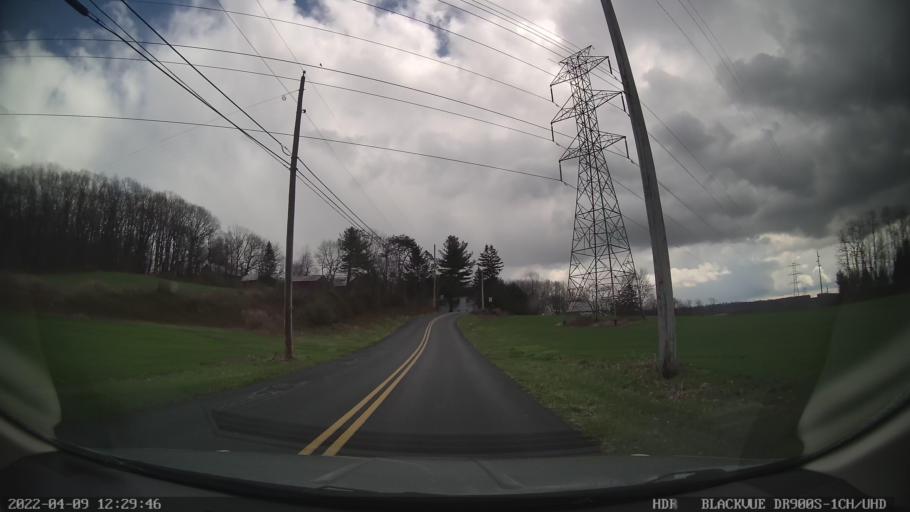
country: US
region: Pennsylvania
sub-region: Berks County
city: Kutztown
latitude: 40.4663
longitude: -75.7638
